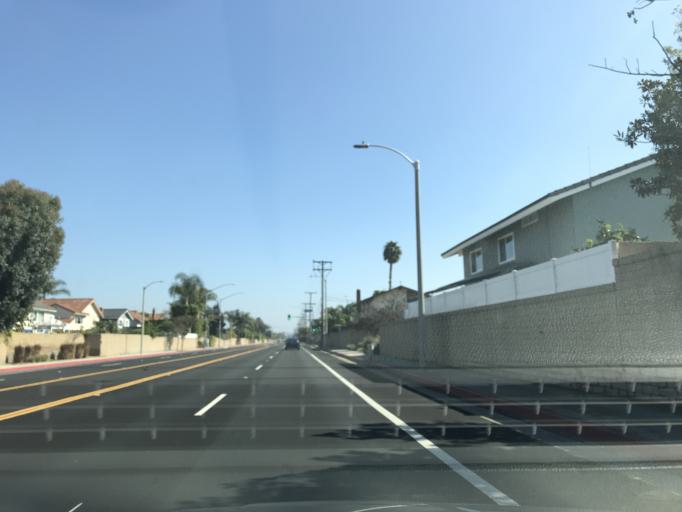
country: US
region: California
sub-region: Orange County
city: Huntington Beach
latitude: 33.6794
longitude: -117.9767
